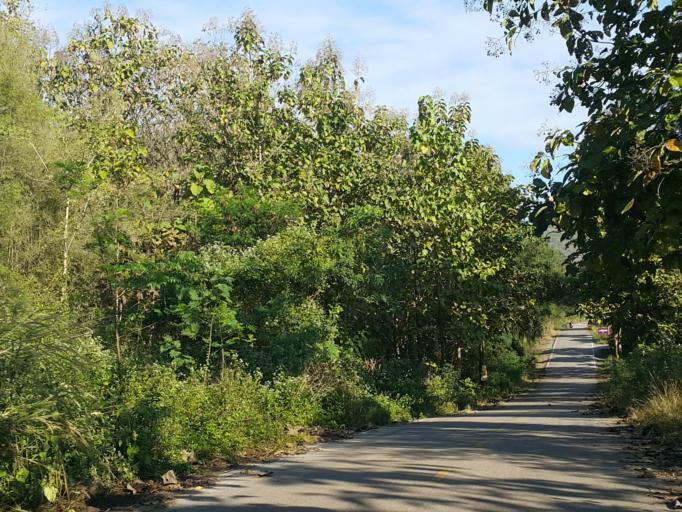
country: TH
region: Lampang
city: Mae Mo
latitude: 18.2653
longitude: 99.6306
